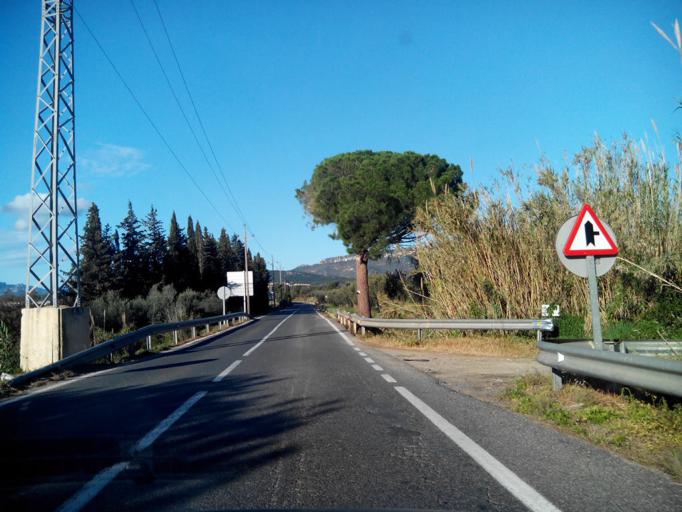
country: ES
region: Catalonia
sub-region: Provincia de Tarragona
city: Riudecanyes
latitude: 41.0969
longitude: 0.9731
